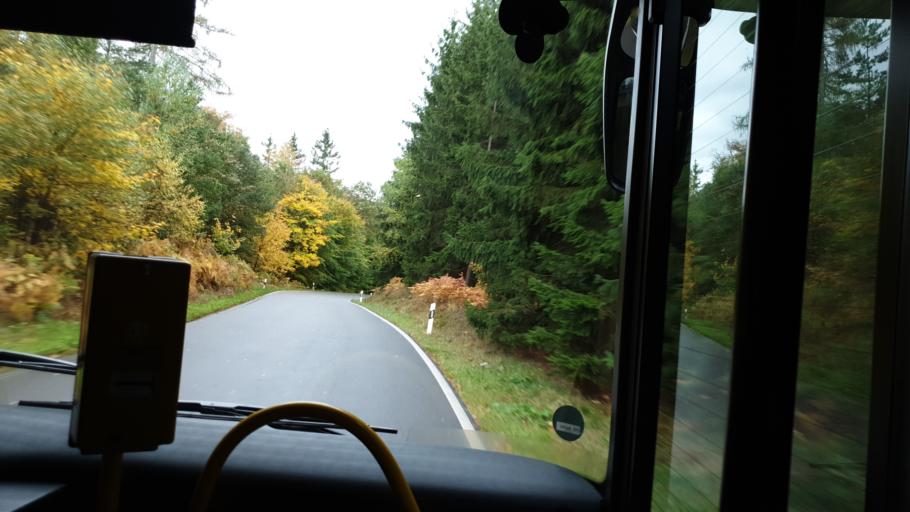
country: DE
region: Saxony
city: Kurort Gohrisch
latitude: 50.8965
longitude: 14.1092
